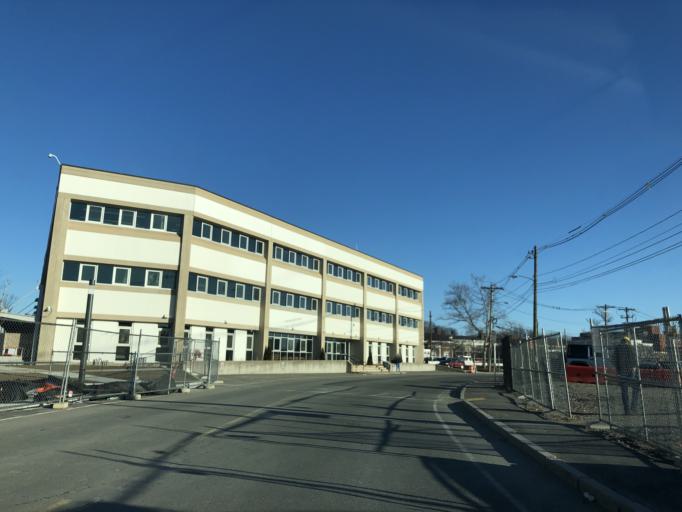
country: US
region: Massachusetts
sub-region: Middlesex County
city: Cambridge
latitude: 42.3625
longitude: -71.1247
